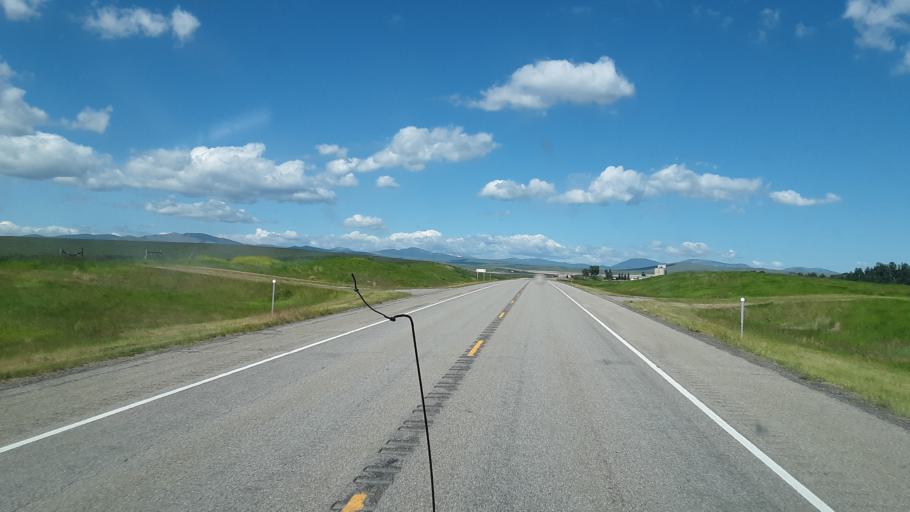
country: US
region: Montana
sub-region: Judith Basin County
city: Stanford
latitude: 47.0761
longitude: -110.1263
